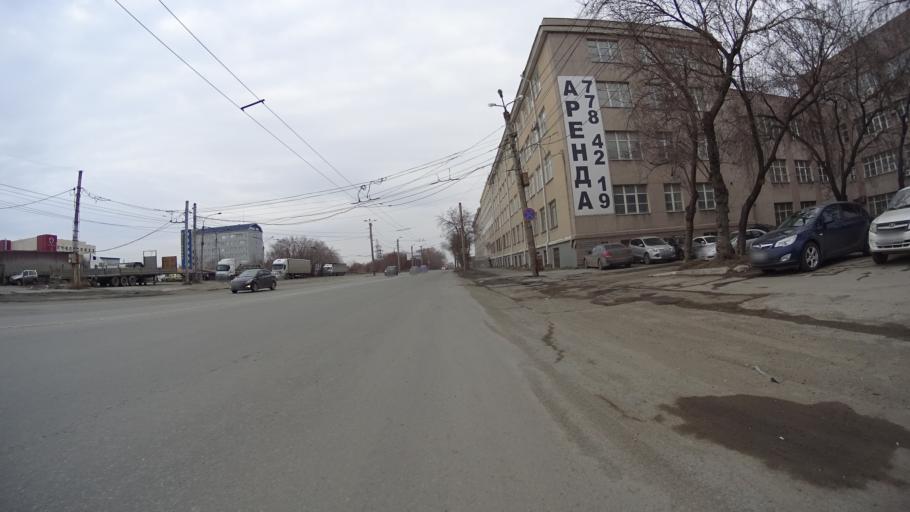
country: RU
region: Chelyabinsk
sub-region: Gorod Chelyabinsk
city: Chelyabinsk
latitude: 55.1589
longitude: 61.4695
